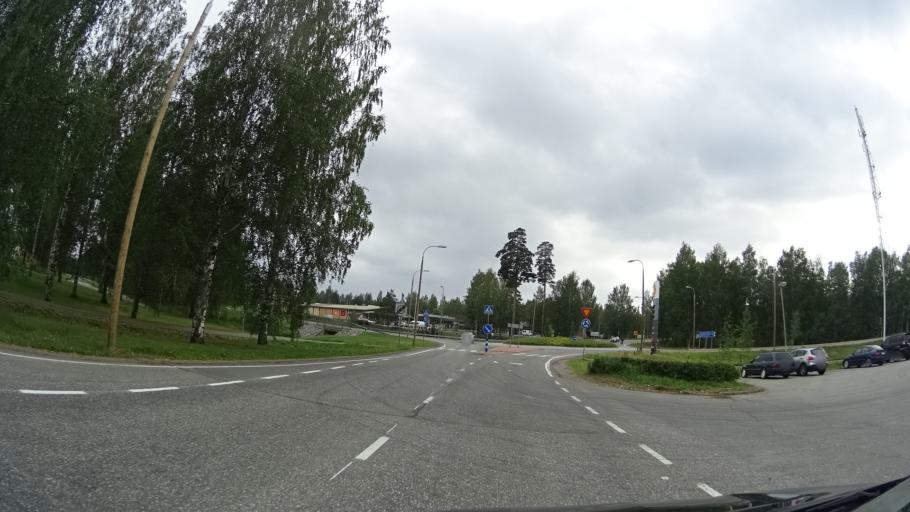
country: FI
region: Southern Savonia
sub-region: Savonlinna
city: Punkaharju
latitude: 61.7563
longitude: 29.3942
